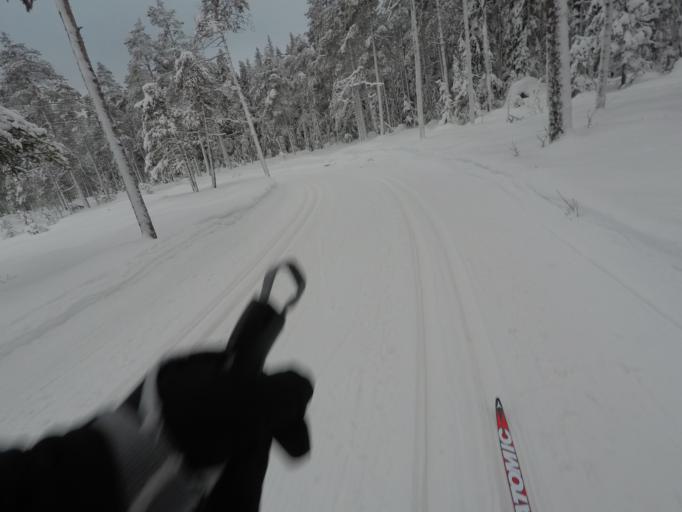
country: SE
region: Vaermland
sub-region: Filipstads Kommun
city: Lesjofors
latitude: 60.1617
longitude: 14.4477
